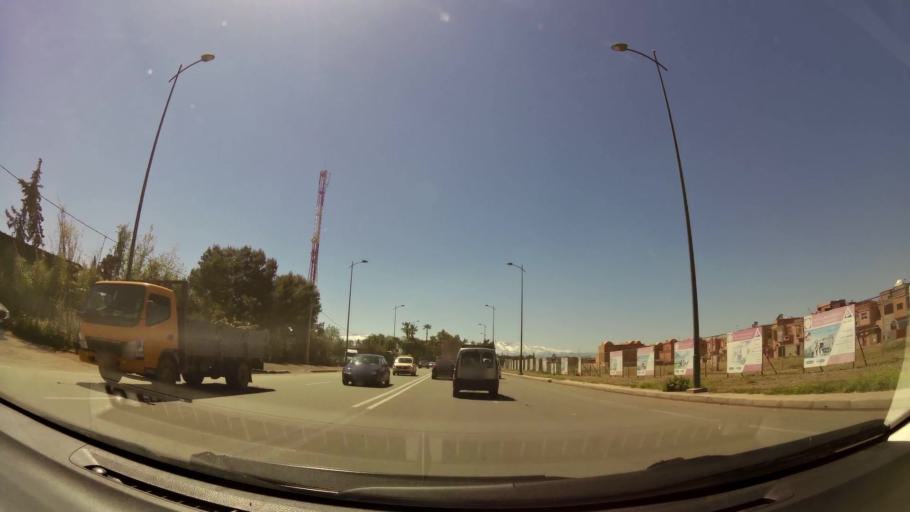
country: MA
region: Marrakech-Tensift-Al Haouz
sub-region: Marrakech
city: Marrakesh
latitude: 31.5719
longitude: -7.9806
